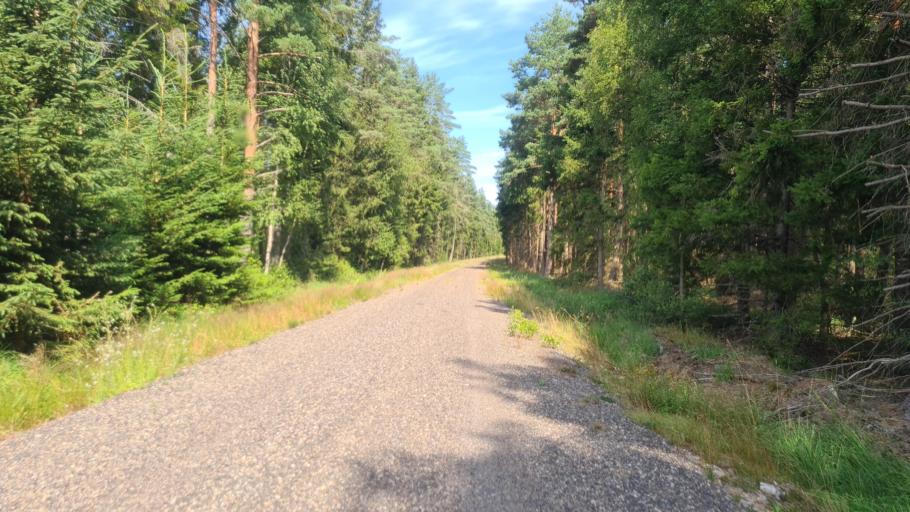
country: SE
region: Kronoberg
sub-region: Ljungby Kommun
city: Lagan
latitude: 56.9562
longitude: 13.9577
